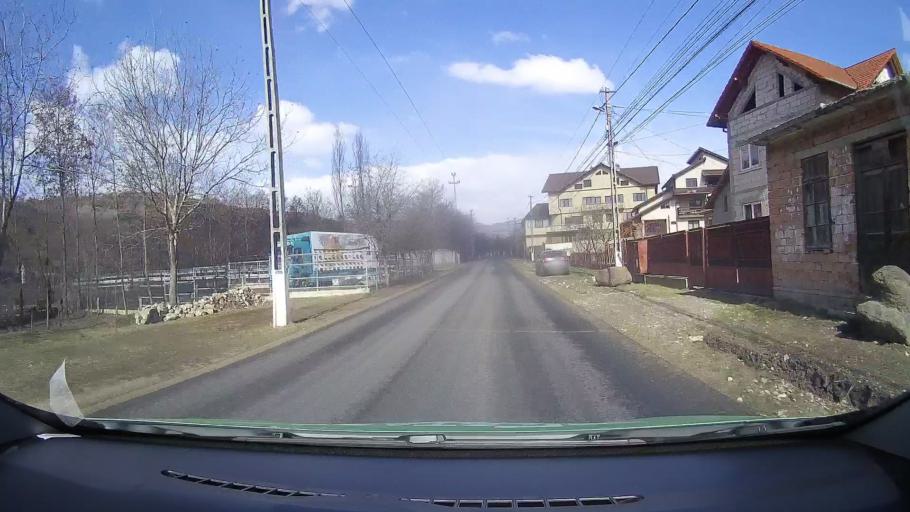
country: RO
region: Dambovita
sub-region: Comuna Runcu
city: Badeni
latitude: 45.1534
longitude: 25.4002
